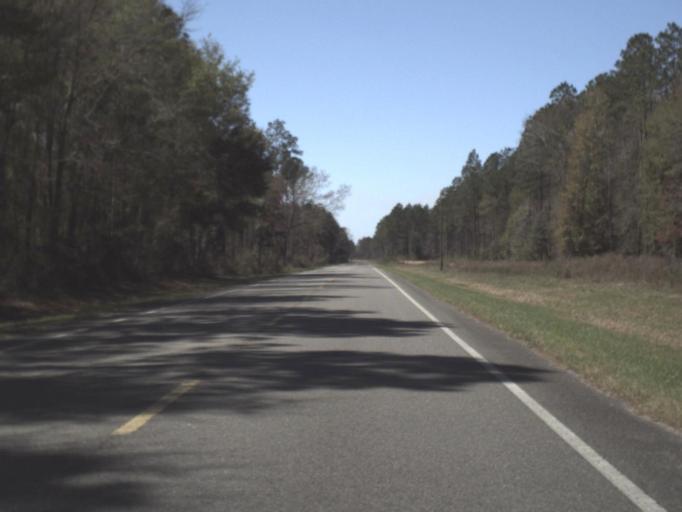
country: US
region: Florida
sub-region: Leon County
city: Woodville
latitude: 30.3405
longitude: -84.0149
